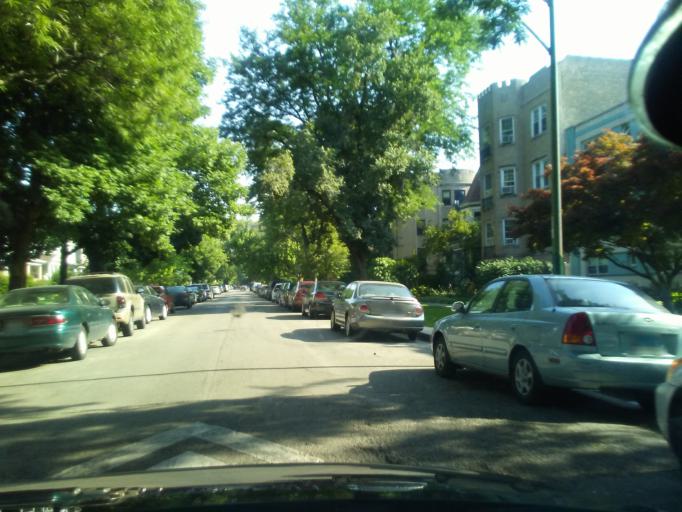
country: US
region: Illinois
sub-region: Cook County
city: Lincolnwood
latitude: 41.9706
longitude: -87.6710
